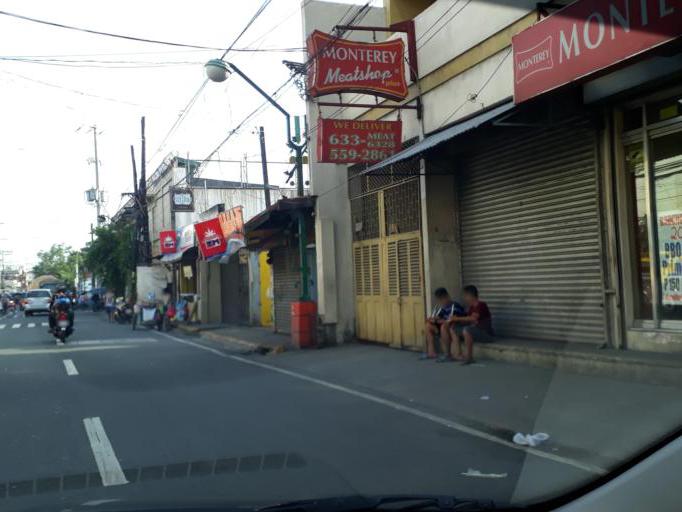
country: PH
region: Metro Manila
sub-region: City of Manila
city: Manila
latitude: 14.6250
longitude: 120.9730
